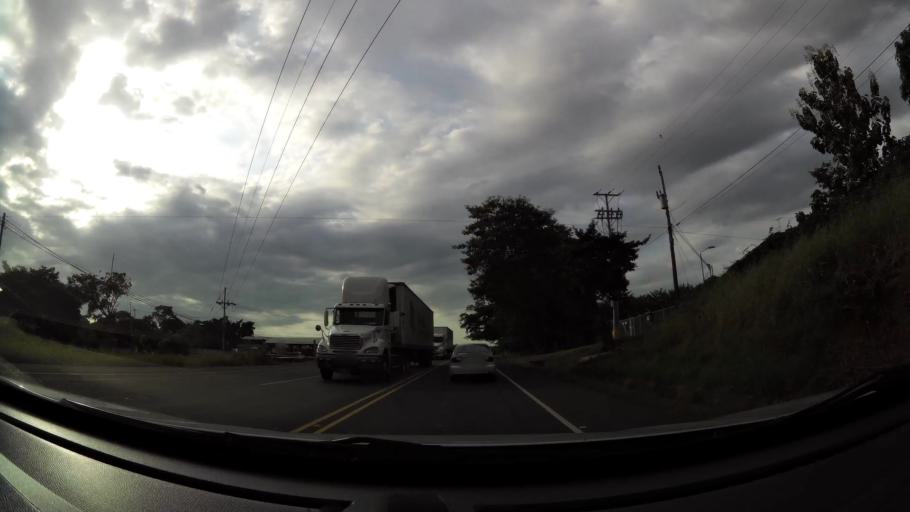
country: CR
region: Puntarenas
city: Esparza
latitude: 9.8937
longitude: -84.6512
